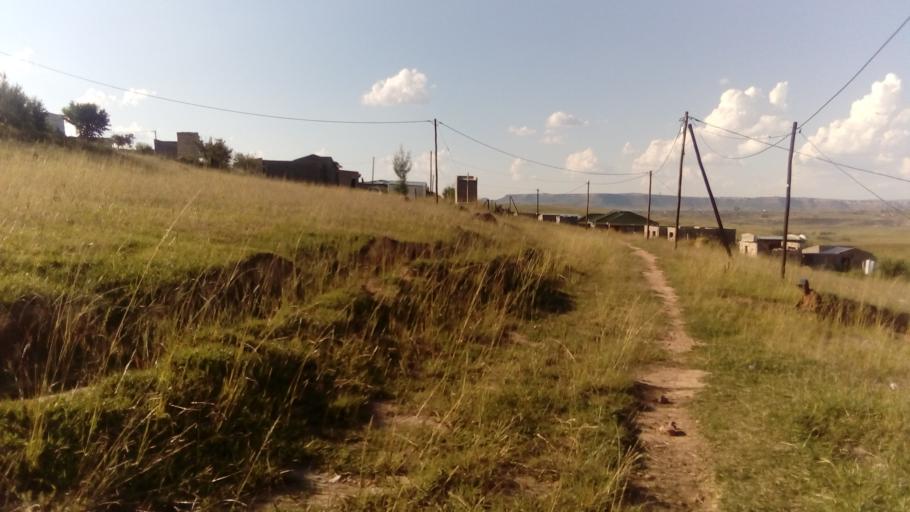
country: LS
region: Berea
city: Teyateyaneng
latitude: -29.1326
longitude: 27.7630
